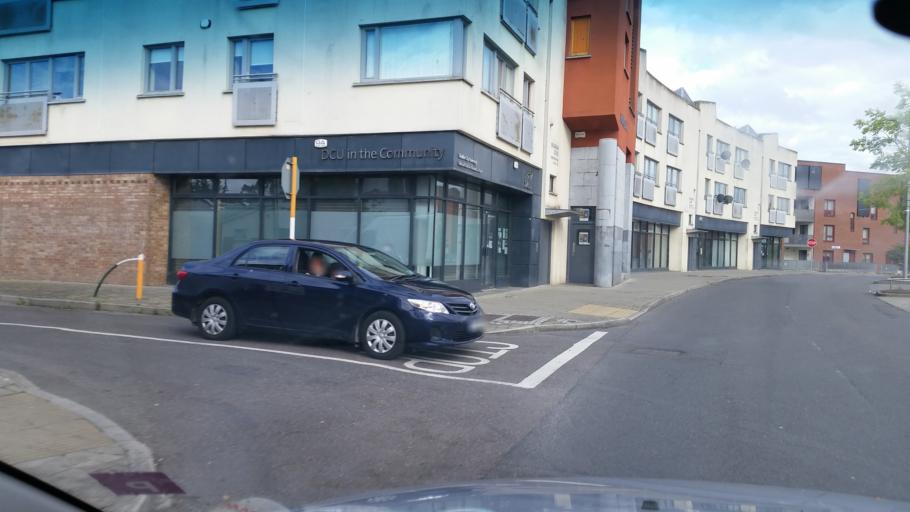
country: IE
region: Leinster
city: Ballymun
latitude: 53.3944
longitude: -6.2583
